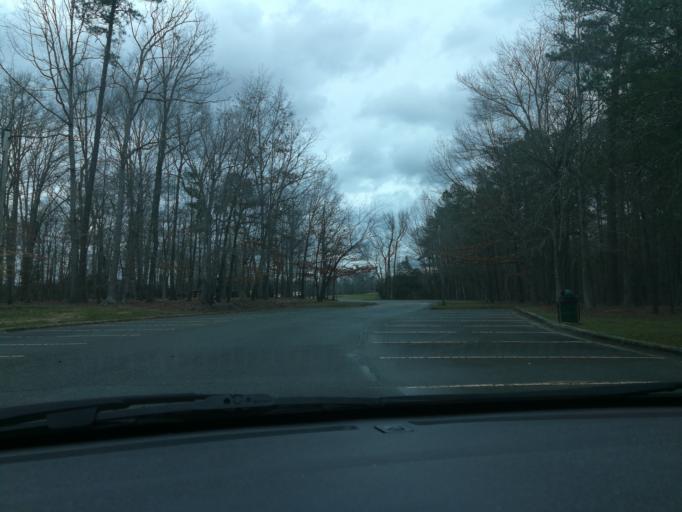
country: US
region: North Carolina
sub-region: Orange County
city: Carrboro
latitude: 35.9233
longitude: -79.1064
